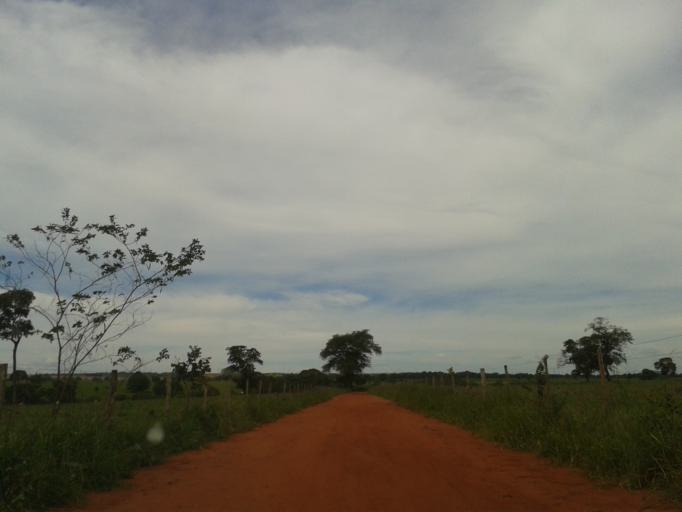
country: BR
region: Minas Gerais
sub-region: Capinopolis
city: Capinopolis
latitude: -18.7924
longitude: -49.8024
